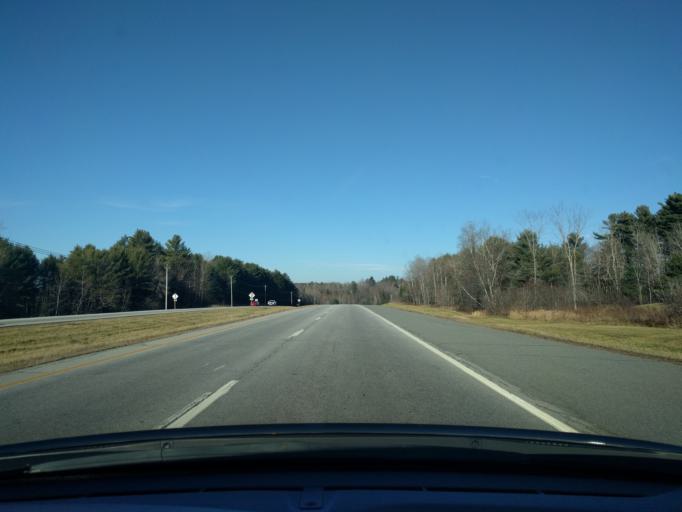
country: US
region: Maine
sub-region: Penobscot County
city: Hampden
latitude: 44.7457
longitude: -68.8458
